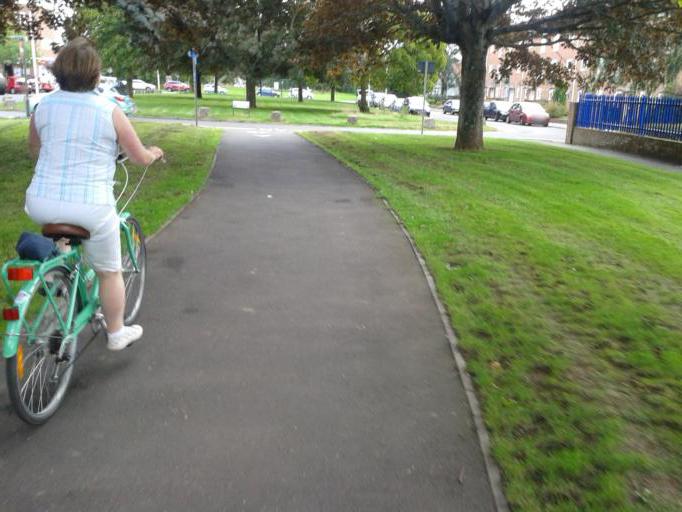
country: GB
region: England
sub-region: Devon
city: Exminster
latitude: 50.6971
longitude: -3.4925
